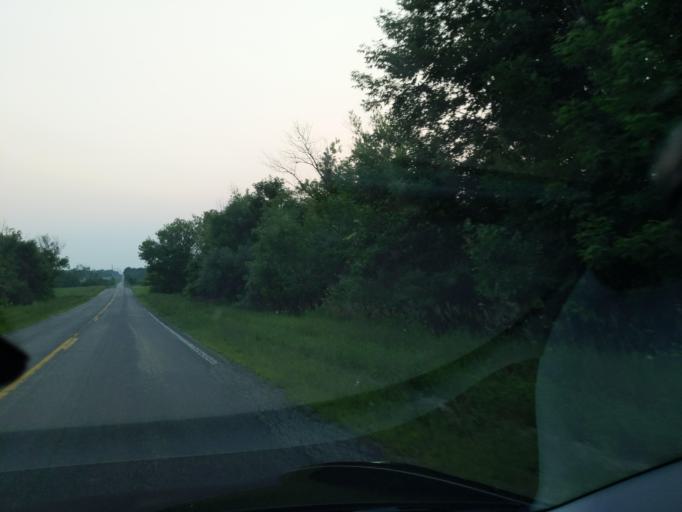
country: US
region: Michigan
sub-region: Jackson County
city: Jackson
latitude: 42.3276
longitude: -84.4308
